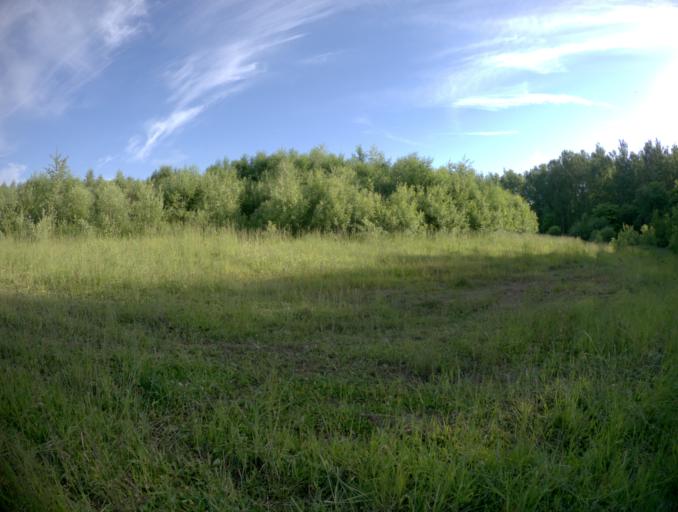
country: RU
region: Vladimir
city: Vorsha
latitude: 56.1519
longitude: 40.2153
